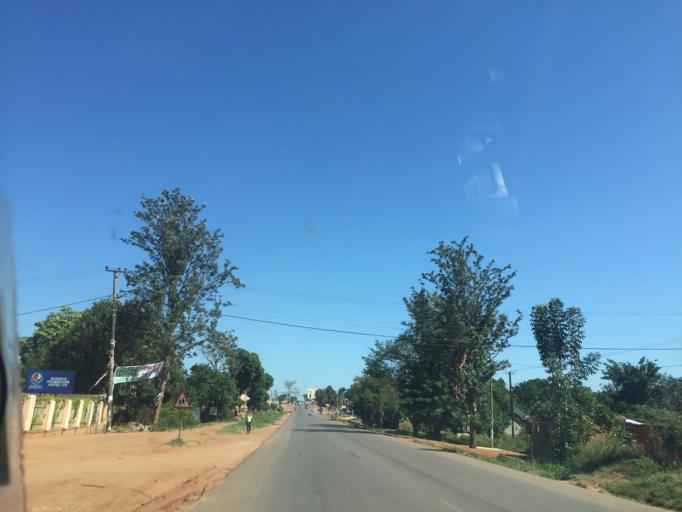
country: UG
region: Central Region
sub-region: Luwero District
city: Luwero
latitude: 0.8233
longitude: 32.5027
